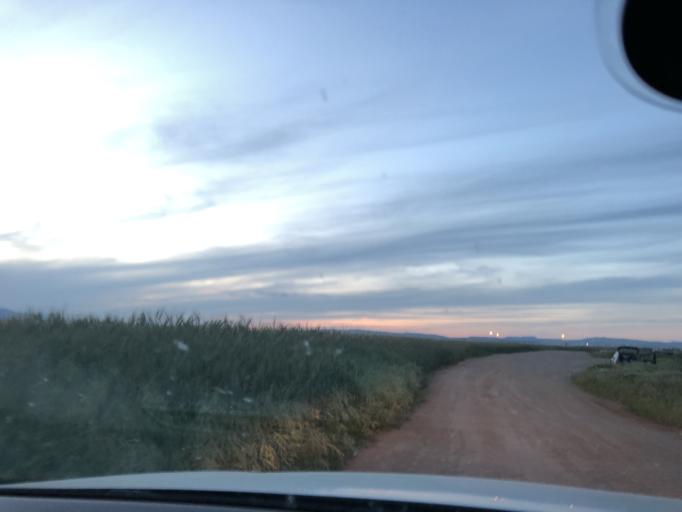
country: CY
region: Larnaka
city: Meneou
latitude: 34.8717
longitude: 33.6378
